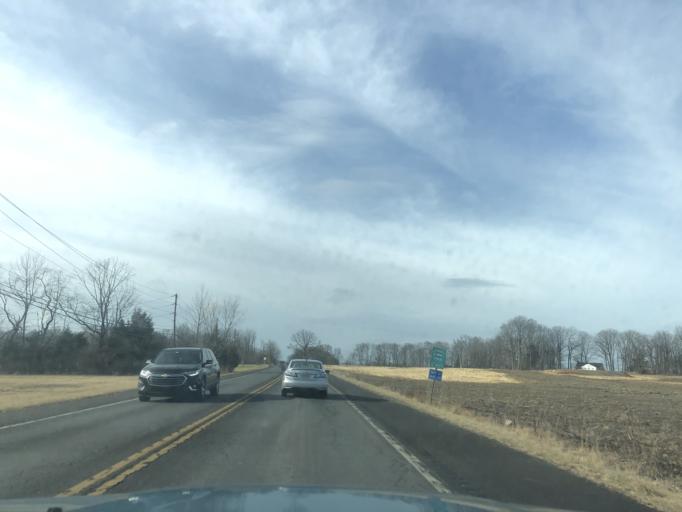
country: US
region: Pennsylvania
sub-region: Bucks County
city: Quakertown
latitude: 40.4416
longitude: -75.3860
